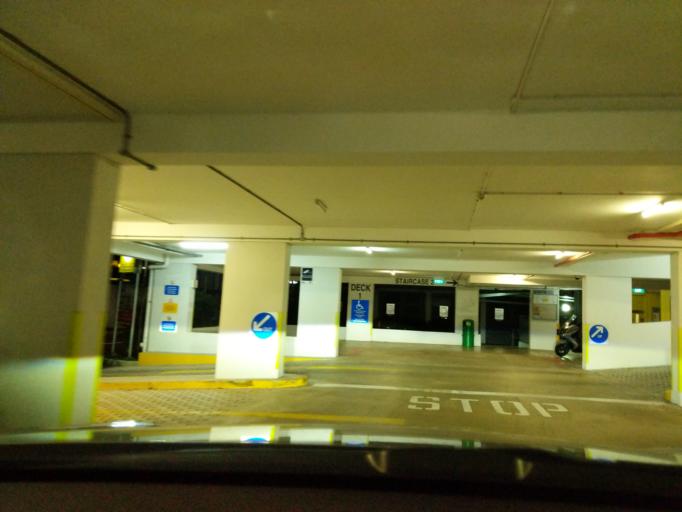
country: SG
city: Singapore
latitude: 1.3361
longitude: 103.9218
